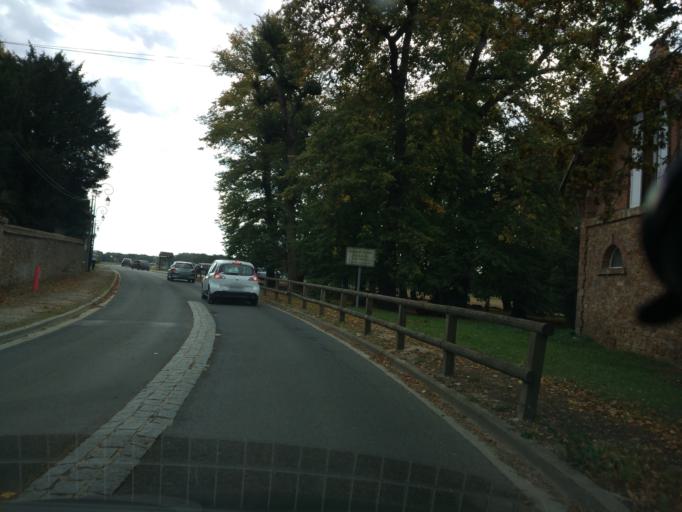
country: FR
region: Ile-de-France
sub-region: Departement de l'Essonne
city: Briis-sous-Forges
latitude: 48.6475
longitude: 2.1196
